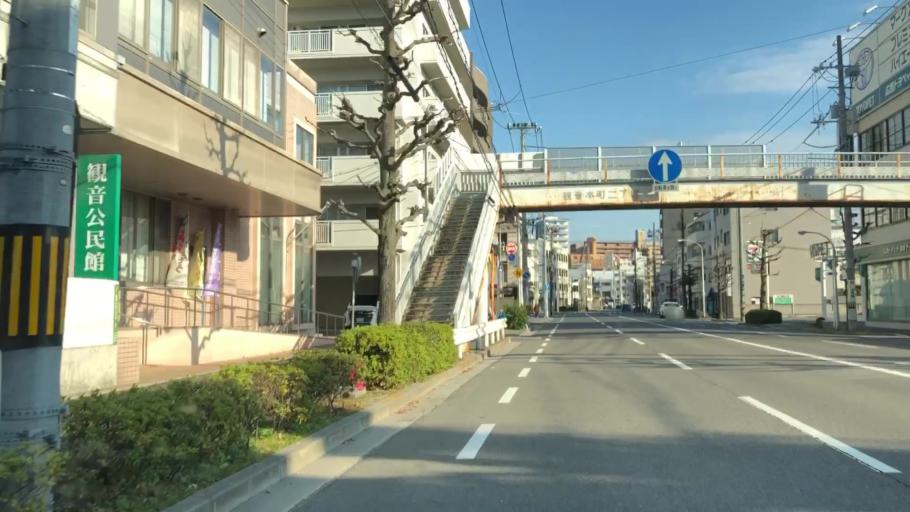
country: JP
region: Hiroshima
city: Hiroshima-shi
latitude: 34.3900
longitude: 132.4369
